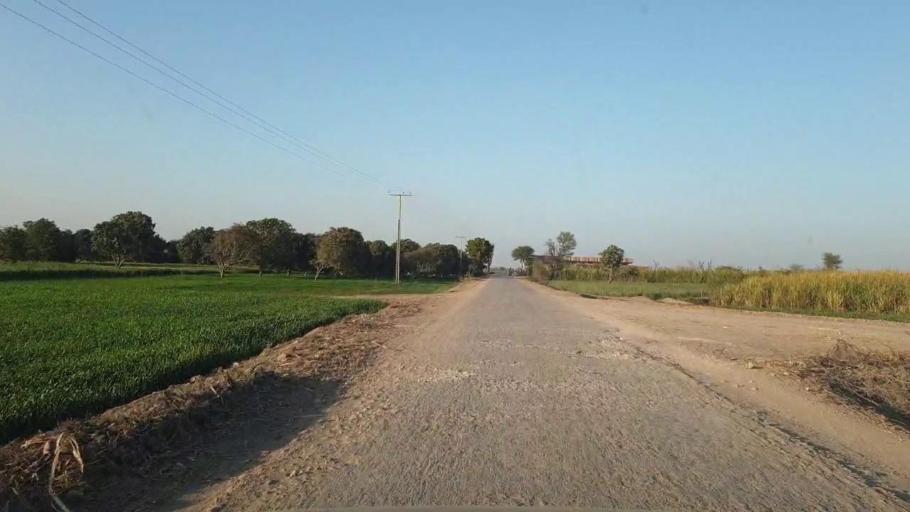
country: PK
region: Sindh
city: Tando Allahyar
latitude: 25.3723
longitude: 68.7479
